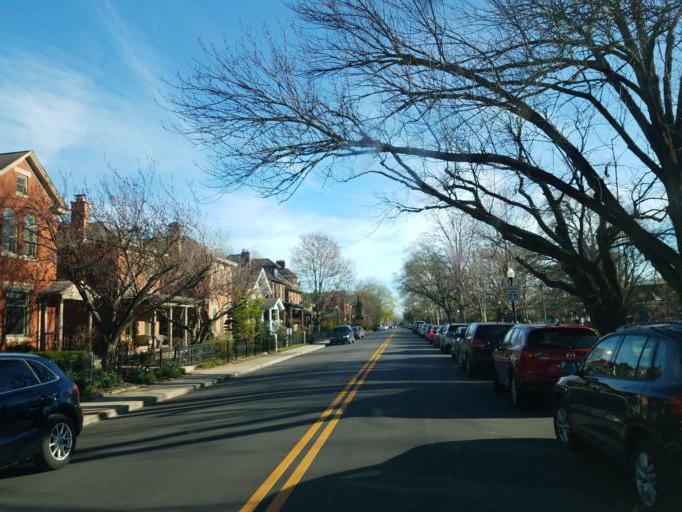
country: US
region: Ohio
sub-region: Franklin County
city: Columbus
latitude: 39.9430
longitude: -82.9904
